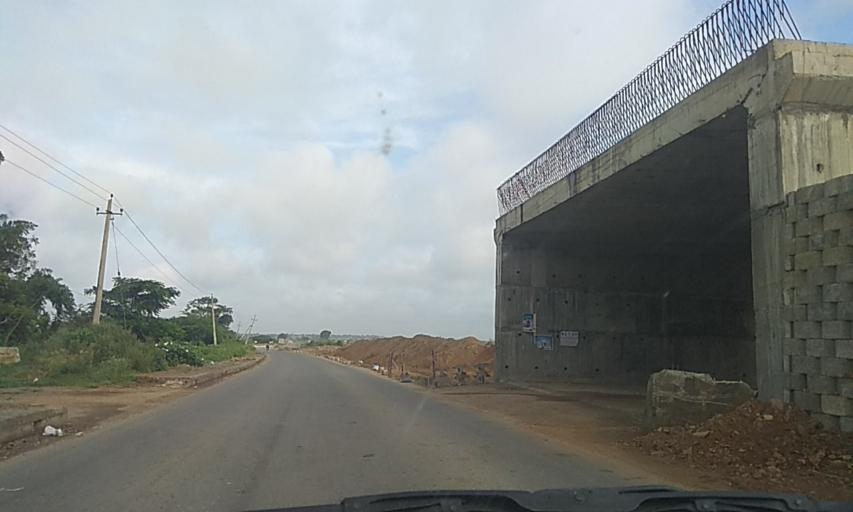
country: IN
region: Karnataka
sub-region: Haveri
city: Haveri
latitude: 14.8541
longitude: 75.3281
